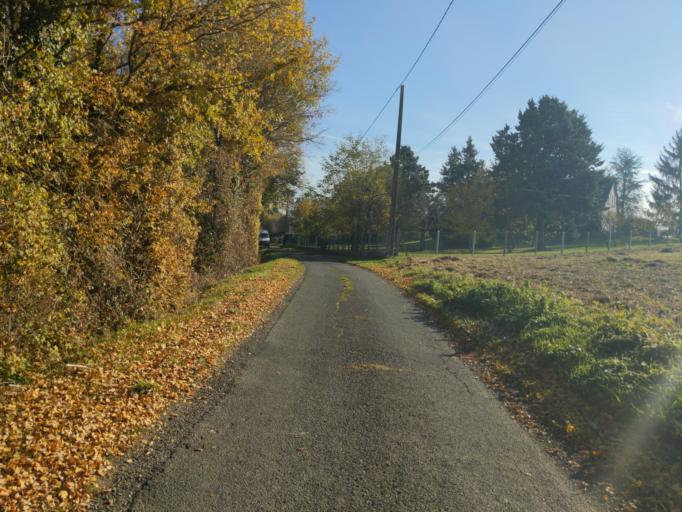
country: FR
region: Centre
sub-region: Departement d'Indre-et-Loire
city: Reugny
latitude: 47.4837
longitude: 0.8630
